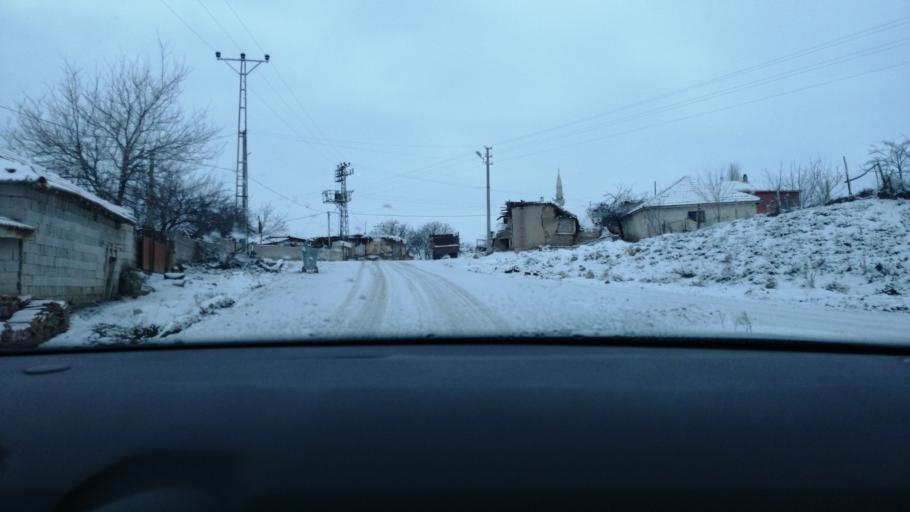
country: TR
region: Aksaray
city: Agacoren
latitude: 38.9352
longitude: 33.9487
